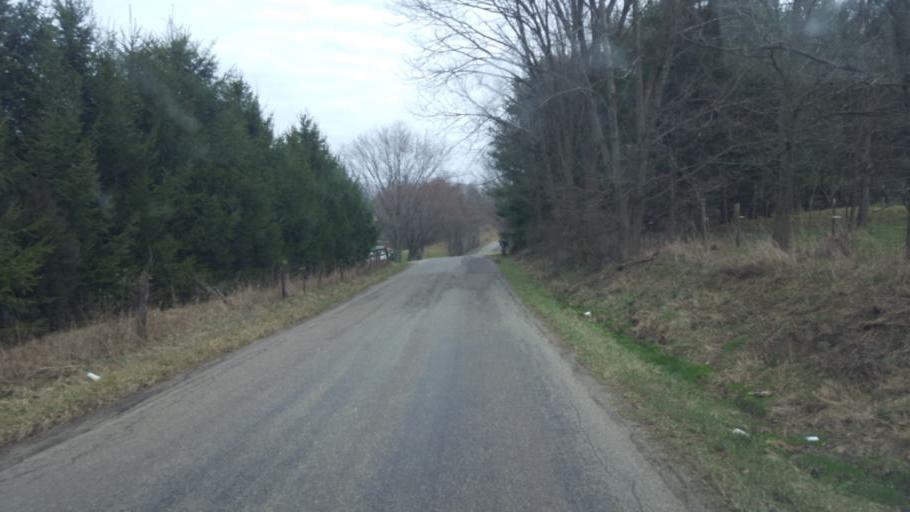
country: US
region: Ohio
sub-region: Sandusky County
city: Bellville
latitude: 40.5639
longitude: -82.3838
